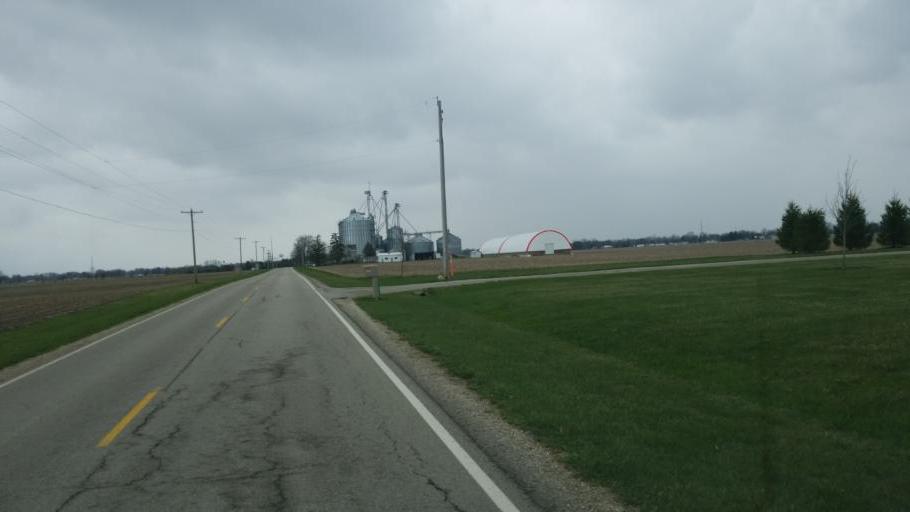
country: US
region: Ohio
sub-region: Union County
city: Richwood
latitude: 40.4243
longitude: -83.2653
